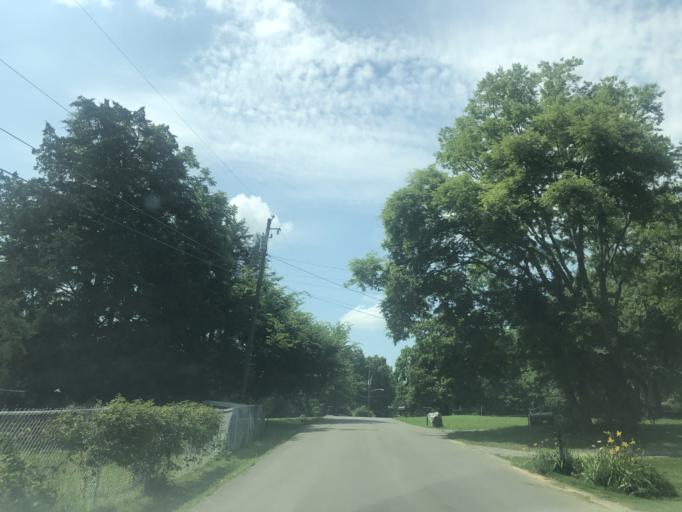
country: US
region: Tennessee
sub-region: Rutherford County
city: La Vergne
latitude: 36.0134
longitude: -86.5868
